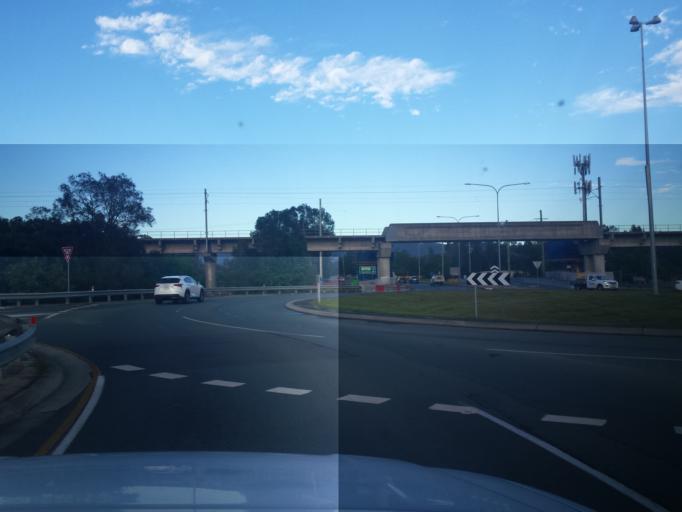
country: AU
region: Queensland
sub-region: Gold Coast
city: Oxenford
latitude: -27.8809
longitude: 153.3326
